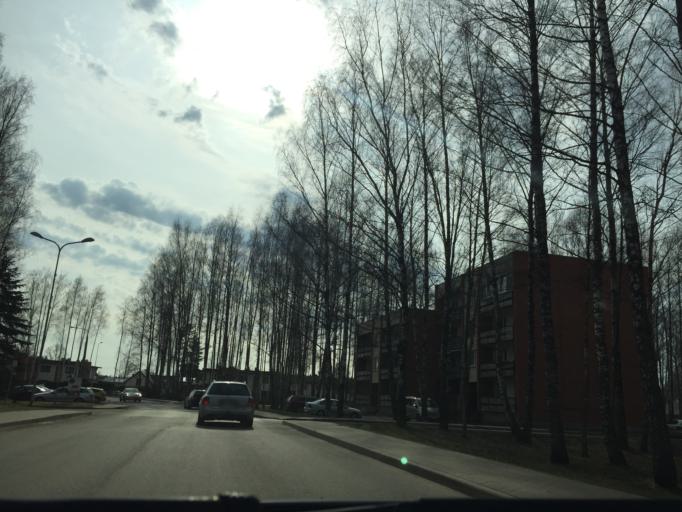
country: LV
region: Kekava
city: Balozi
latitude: 56.8800
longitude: 24.1470
